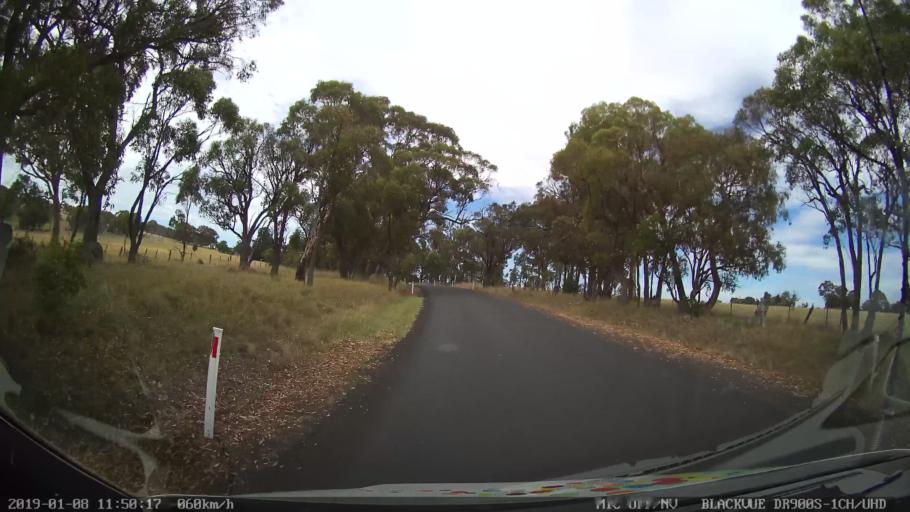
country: AU
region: New South Wales
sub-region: Armidale Dumaresq
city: Armidale
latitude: -30.3812
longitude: 151.5575
